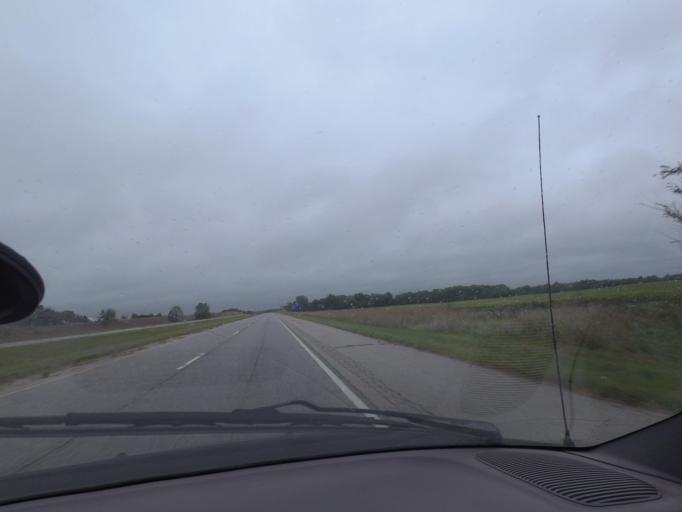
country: US
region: Illinois
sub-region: Pike County
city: Pittsfield
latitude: 39.6713
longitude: -90.8001
